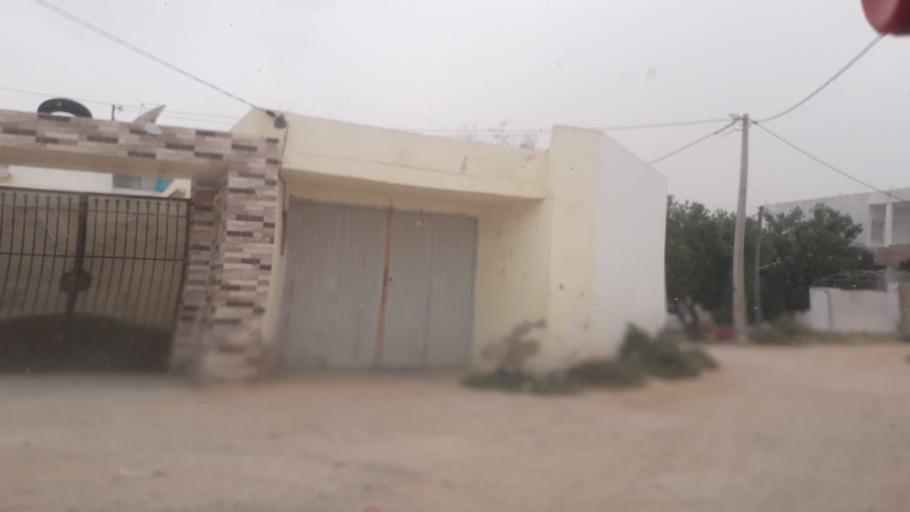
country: TN
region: Safaqis
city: Al Qarmadah
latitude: 34.7963
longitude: 10.7656
